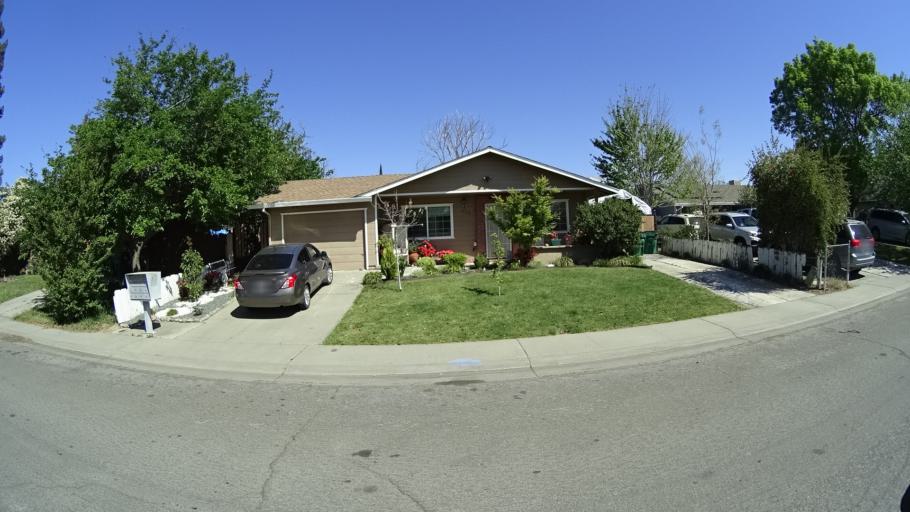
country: US
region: California
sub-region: Glenn County
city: Orland
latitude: 39.7570
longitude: -122.1984
